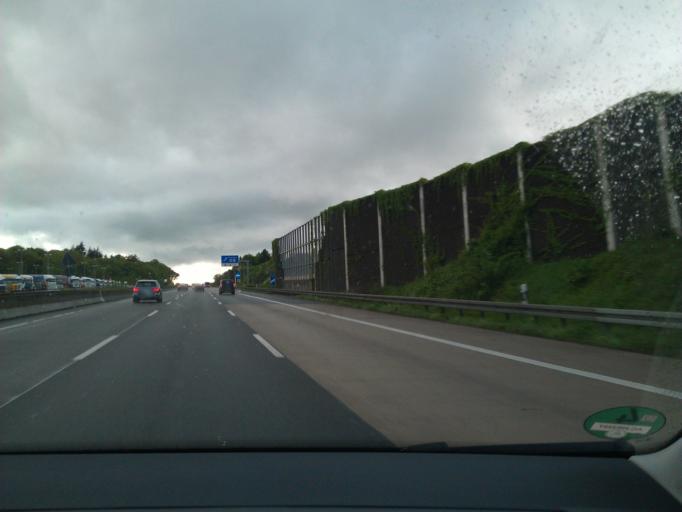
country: DE
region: North Rhine-Westphalia
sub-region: Regierungsbezirk Koln
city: Frechen
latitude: 50.9294
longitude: 6.7828
